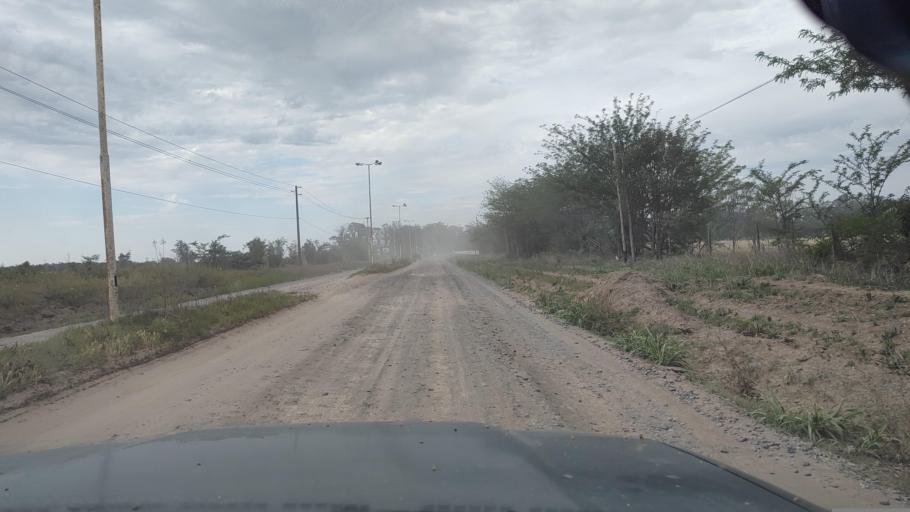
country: AR
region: Buenos Aires
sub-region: Partido de Lujan
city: Lujan
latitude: -34.5483
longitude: -59.0832
